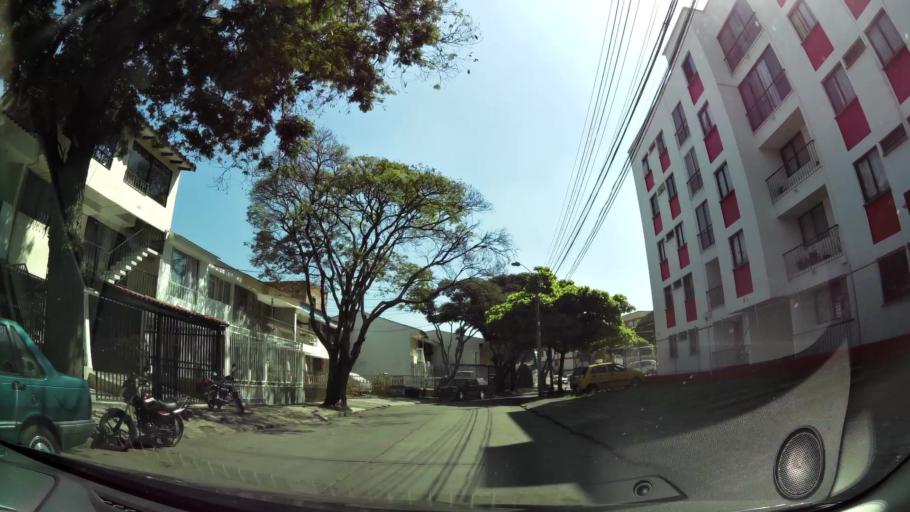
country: CO
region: Valle del Cauca
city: Cali
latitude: 3.4299
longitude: -76.5283
